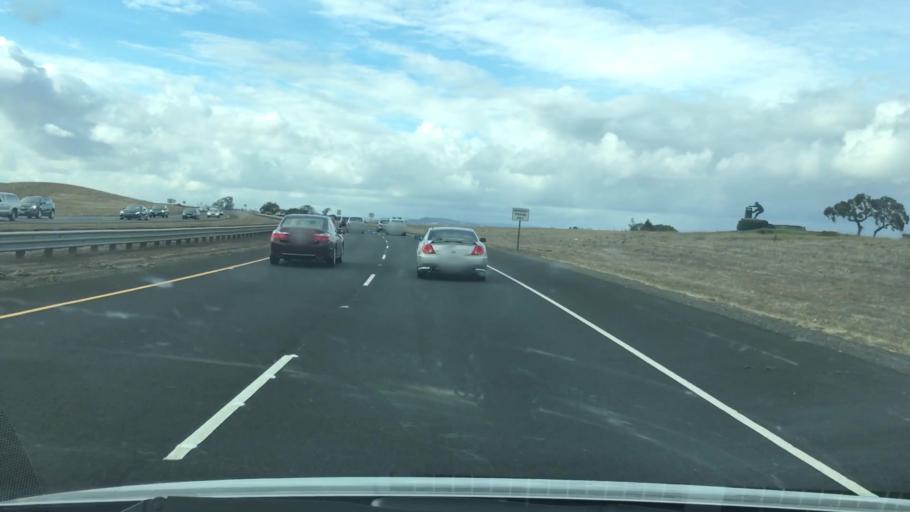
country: US
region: California
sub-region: Napa County
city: Napa
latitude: 38.2429
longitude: -122.2723
